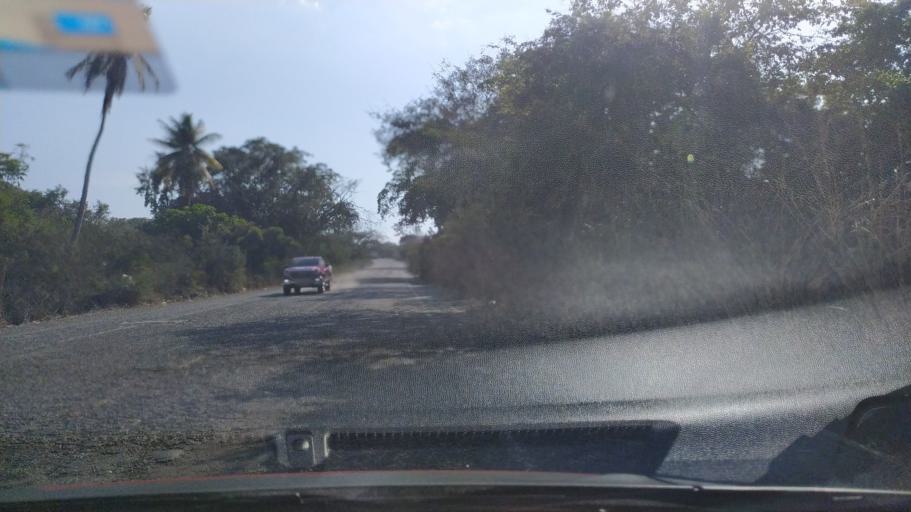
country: MX
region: Michoacan
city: Coahuayana Viejo
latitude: 18.6519
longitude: -103.6717
